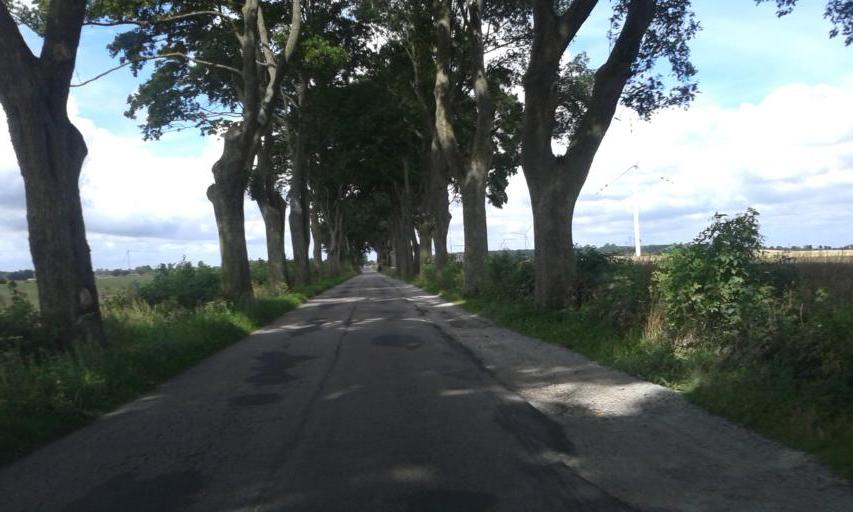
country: PL
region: West Pomeranian Voivodeship
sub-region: Powiat slawienski
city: Slawno
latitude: 54.3206
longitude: 16.5910
